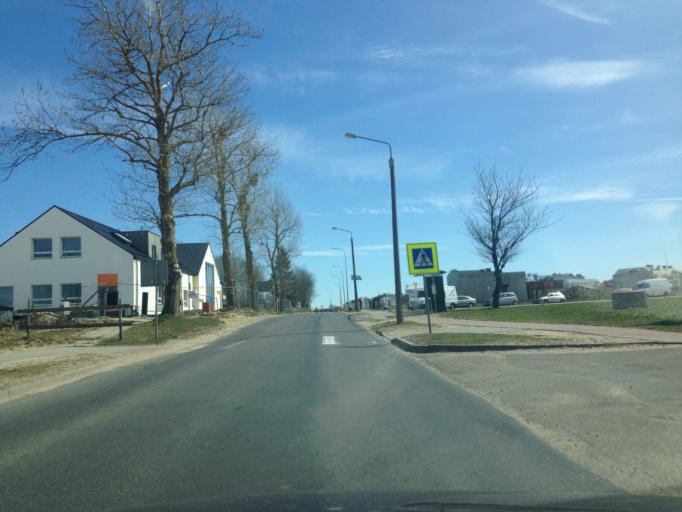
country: PL
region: Pomeranian Voivodeship
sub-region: Powiat wejherowski
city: Bojano
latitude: 54.4901
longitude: 18.4246
